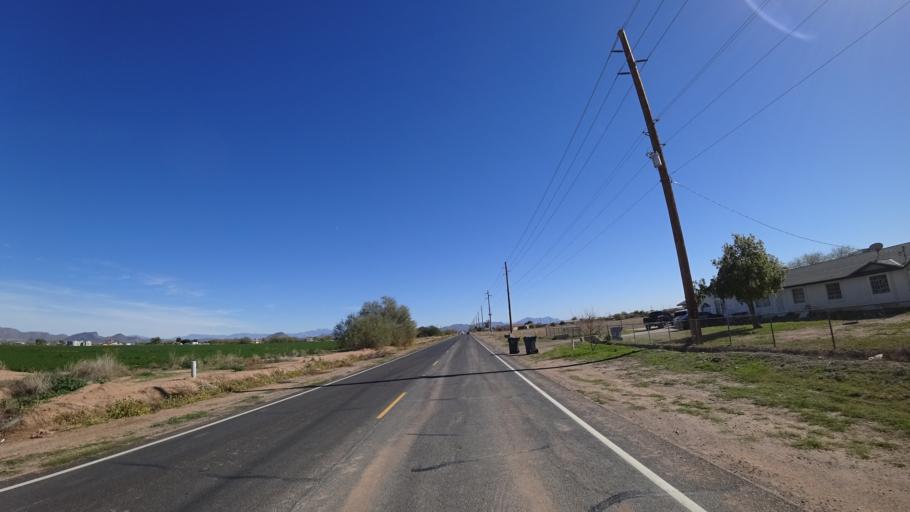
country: US
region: Arizona
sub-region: Maricopa County
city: Scottsdale
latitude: 33.4951
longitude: -111.8532
